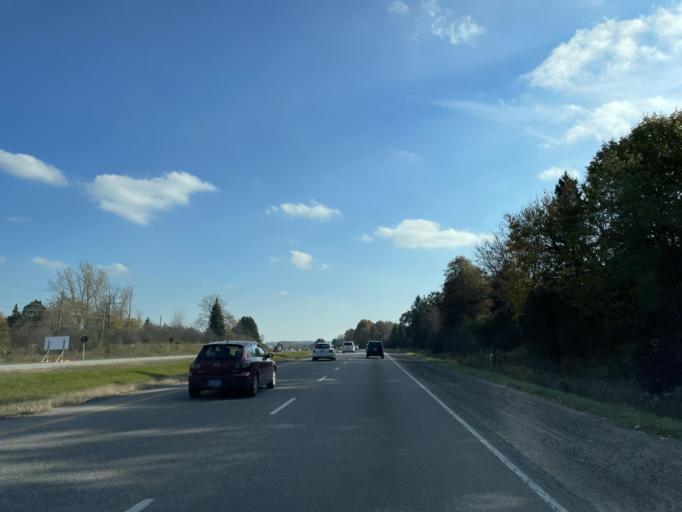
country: CA
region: Ontario
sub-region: Wellington County
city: Guelph
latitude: 43.5113
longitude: -80.2408
